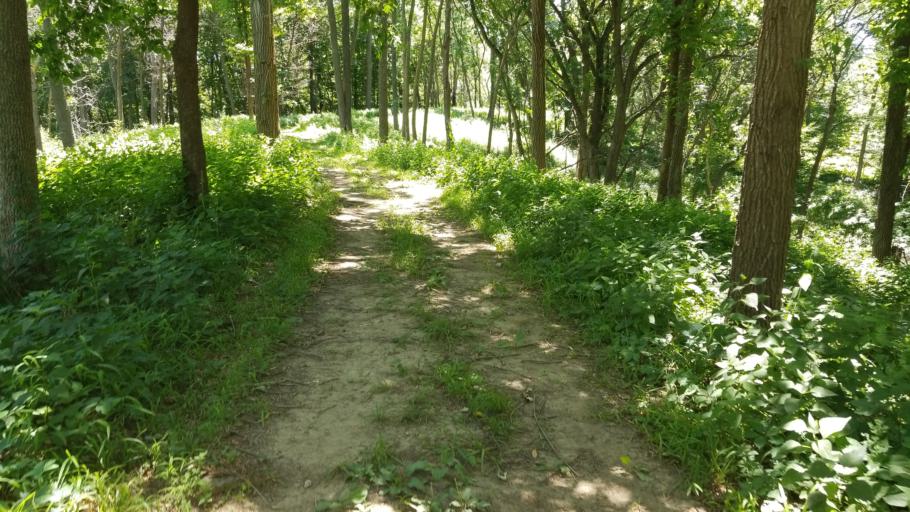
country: US
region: Iowa
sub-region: Pottawattamie County
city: Carter Lake
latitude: 41.3968
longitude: -95.9535
